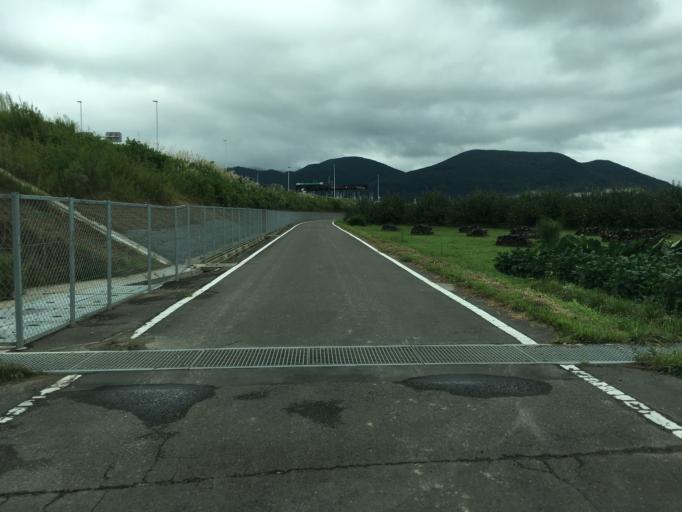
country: JP
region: Fukushima
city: Fukushima-shi
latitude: 37.7903
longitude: 140.4164
